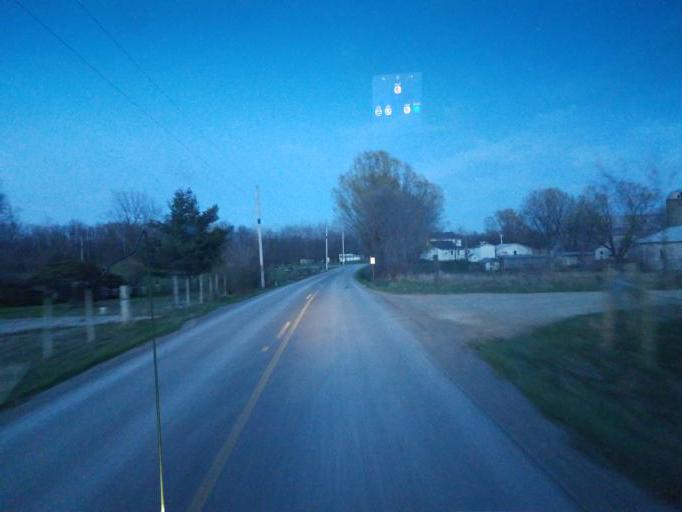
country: US
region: Ohio
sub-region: Logan County
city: De Graff
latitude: 40.3549
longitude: -83.9430
